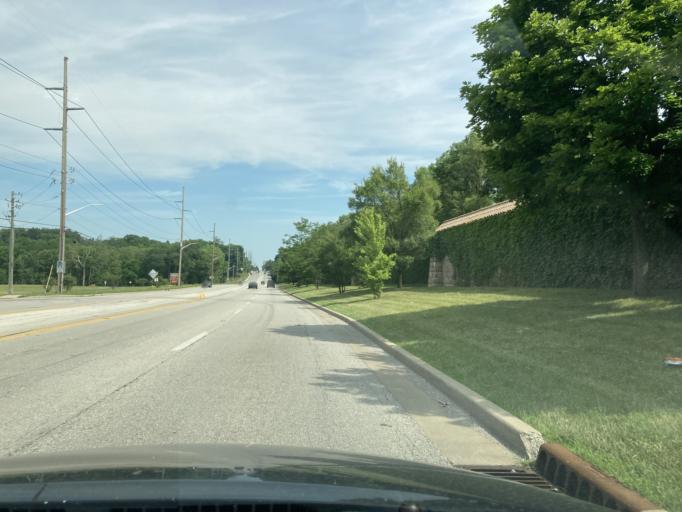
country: US
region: Indiana
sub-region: Marion County
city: Broad Ripple
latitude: 39.8336
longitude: -86.1850
